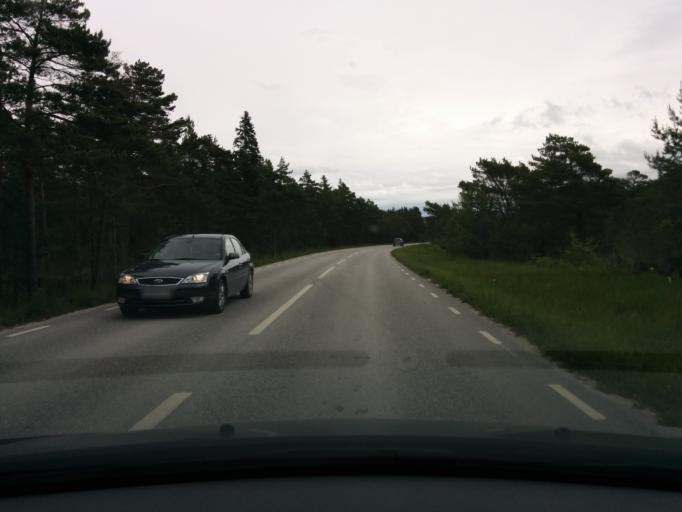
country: SE
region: Gotland
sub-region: Gotland
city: Slite
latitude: 57.6843
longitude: 18.7777
